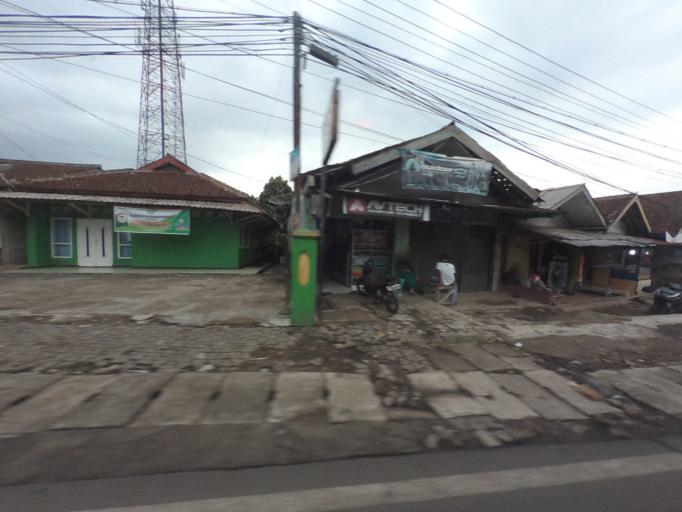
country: ID
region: West Java
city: Cicurug
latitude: -6.8445
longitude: 106.7610
